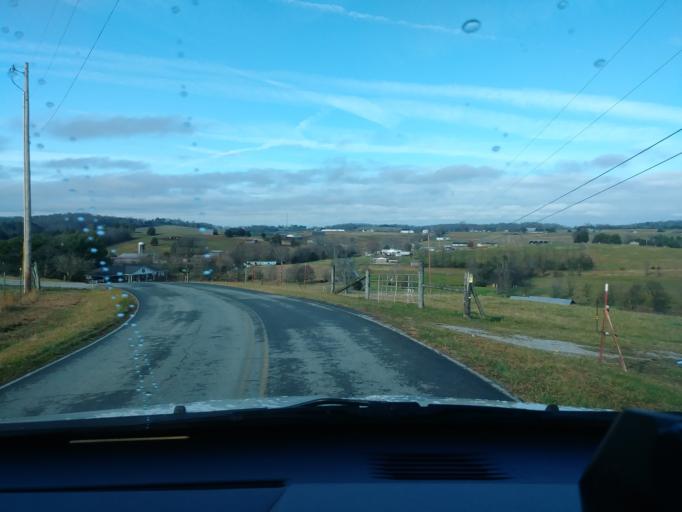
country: US
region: Tennessee
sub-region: Greene County
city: Greeneville
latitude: 36.0899
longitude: -82.9120
